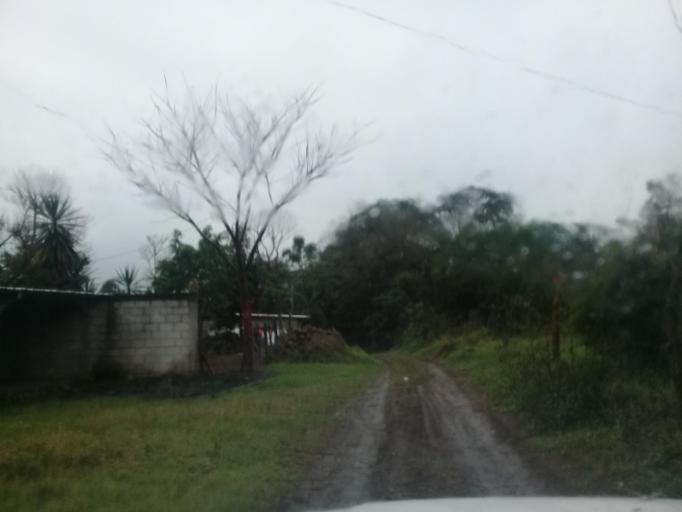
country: MX
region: Veracruz
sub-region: Cordoba
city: San Jose de Tapia
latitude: 18.8504
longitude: -96.9507
